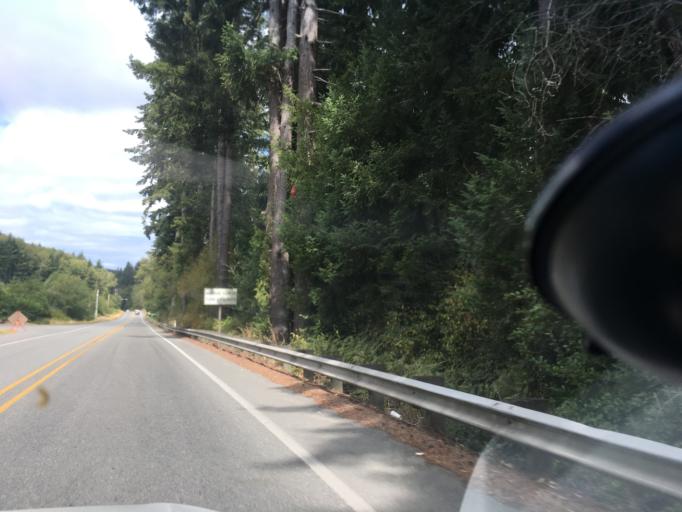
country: US
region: Washington
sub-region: Kitsap County
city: Kingston
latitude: 47.8055
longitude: -122.5722
